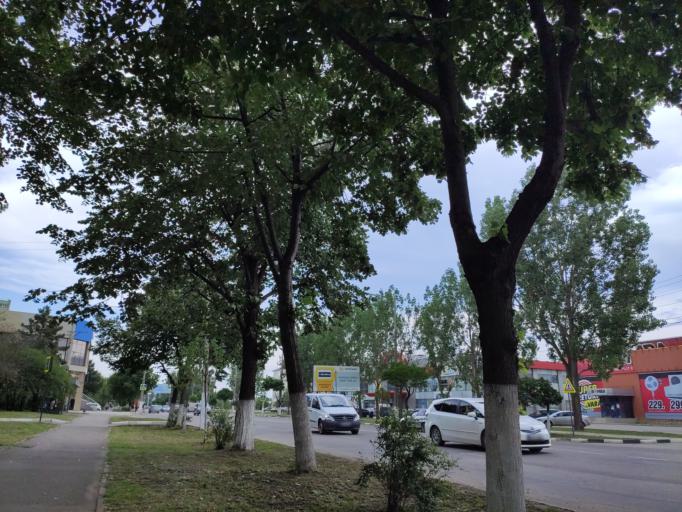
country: MD
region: Balti
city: Balti
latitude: 47.7624
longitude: 27.9410
